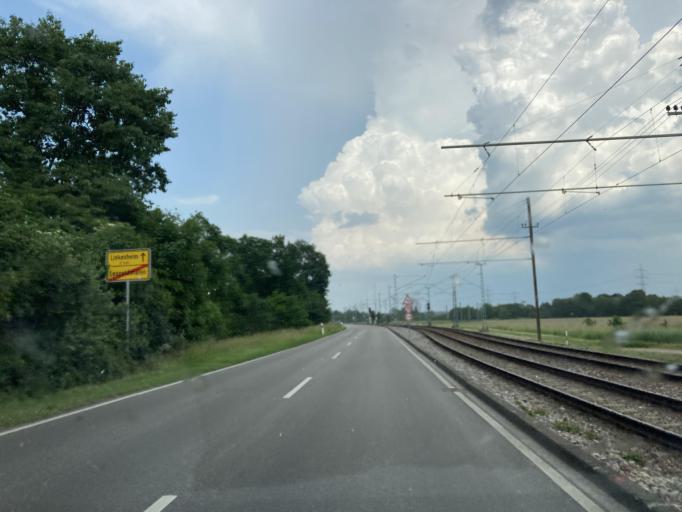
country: DE
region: Baden-Wuerttemberg
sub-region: Karlsruhe Region
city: Eggenstein-Leopoldshafen
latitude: 49.1015
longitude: 8.4045
